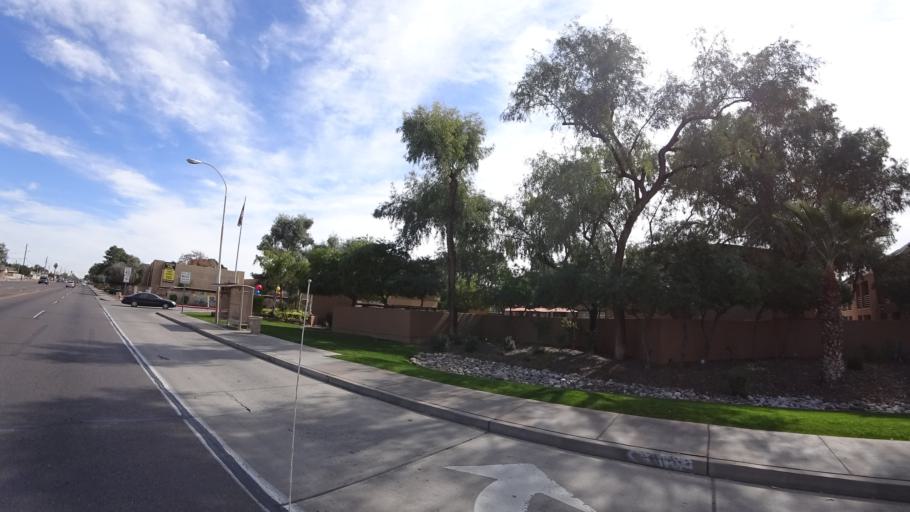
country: US
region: Arizona
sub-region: Maricopa County
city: Glendale
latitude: 33.4804
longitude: -112.1947
